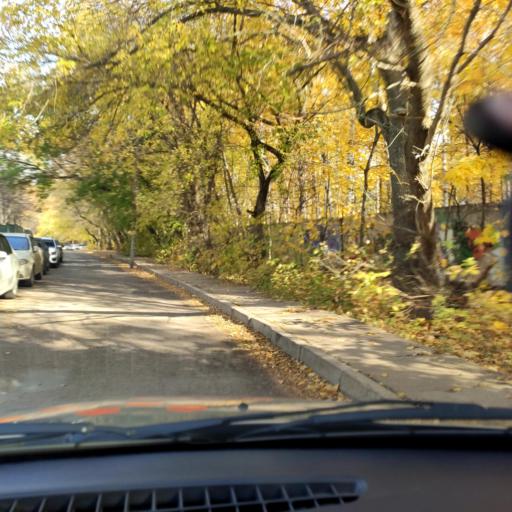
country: RU
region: Bashkortostan
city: Ufa
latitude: 54.7154
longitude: 56.0147
